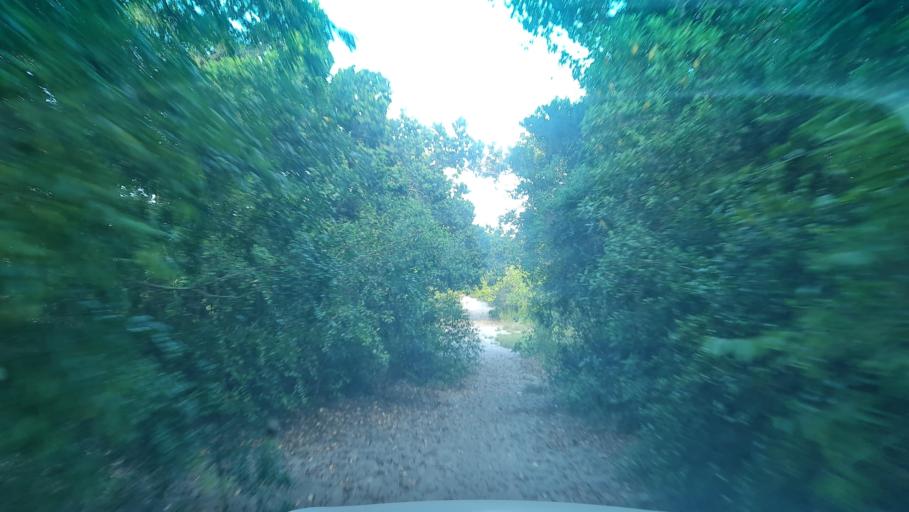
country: MZ
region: Gaza
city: Macia
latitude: -25.2278
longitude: 33.0195
